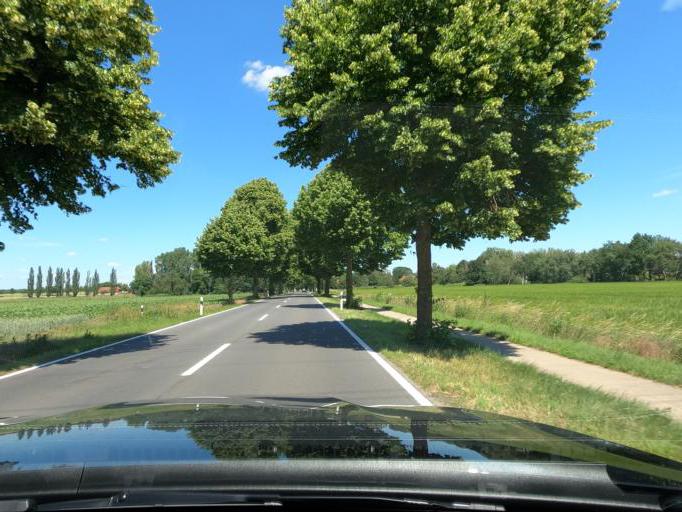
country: DE
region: Lower Saxony
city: Lehrte
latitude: 52.4116
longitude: 9.9760
